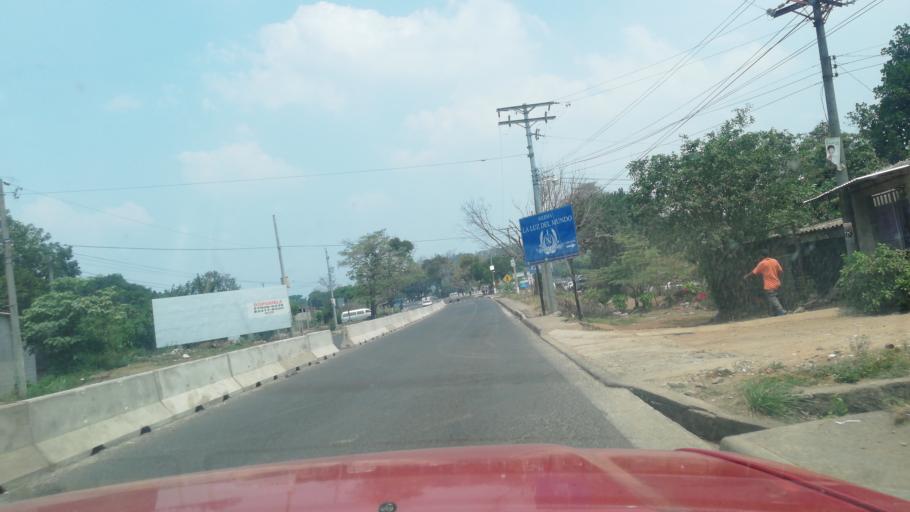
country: SV
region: Santa Ana
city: Santa Ana
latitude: 13.9753
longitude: -89.5879
